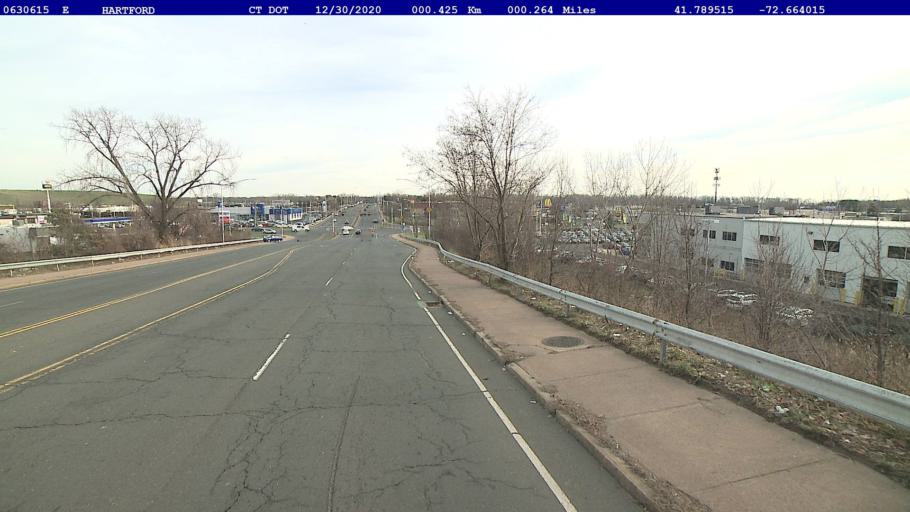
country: US
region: Connecticut
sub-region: Hartford County
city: Hartford
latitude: 41.7895
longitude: -72.6640
